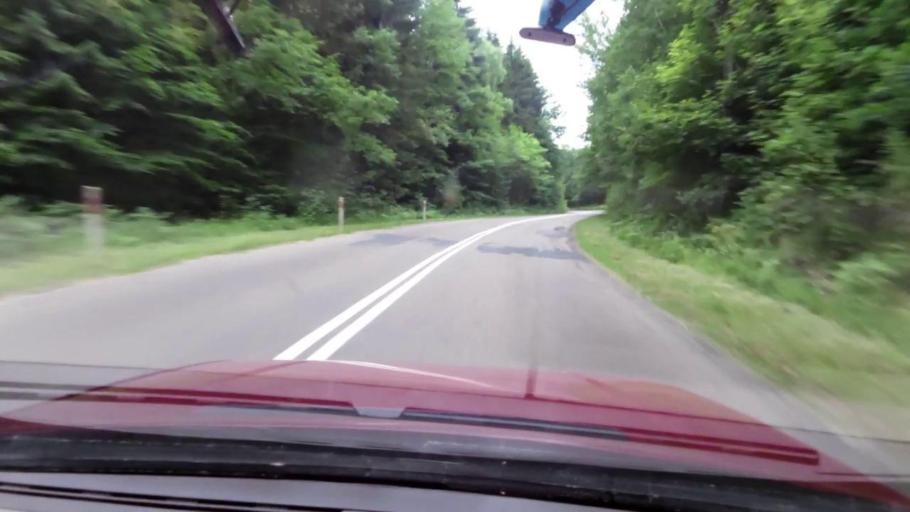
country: PL
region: West Pomeranian Voivodeship
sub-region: Powiat koszalinski
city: Sianow
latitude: 54.1887
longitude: 16.2791
